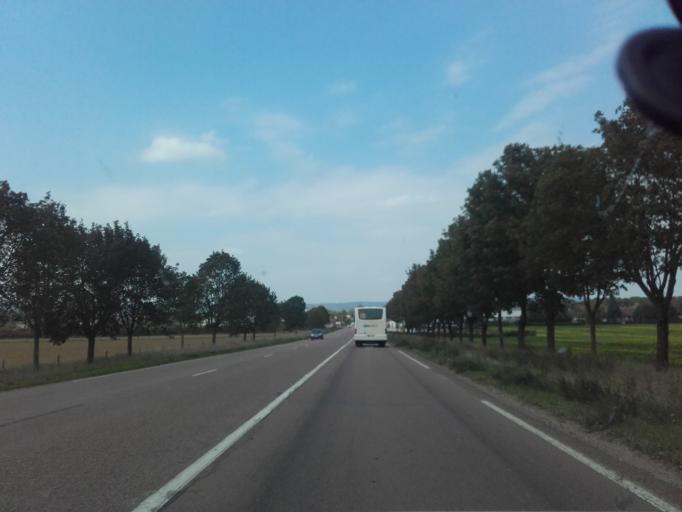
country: FR
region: Bourgogne
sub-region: Departement de Saone-et-Loire
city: Chagny
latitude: 46.8944
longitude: 4.7644
